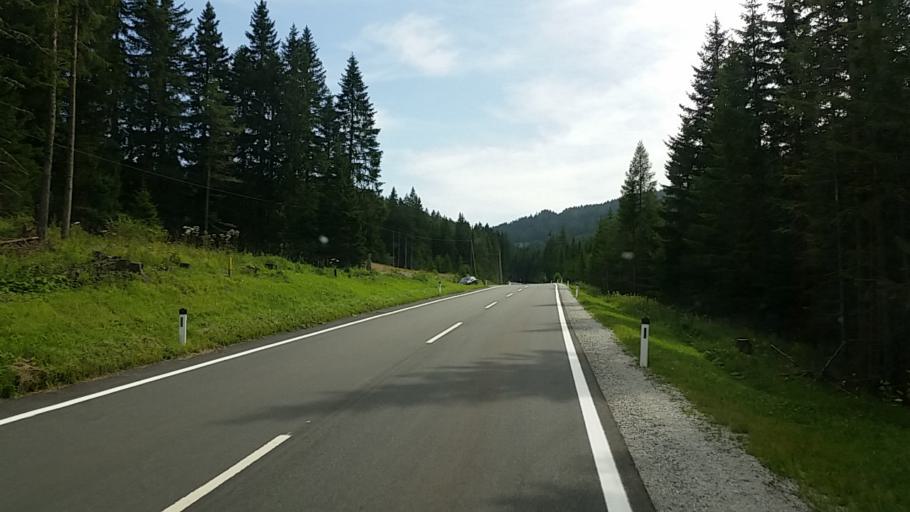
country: AT
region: Salzburg
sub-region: Politischer Bezirk Tamsweg
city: Sankt Michael im Lungau
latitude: 47.0742
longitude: 13.6175
